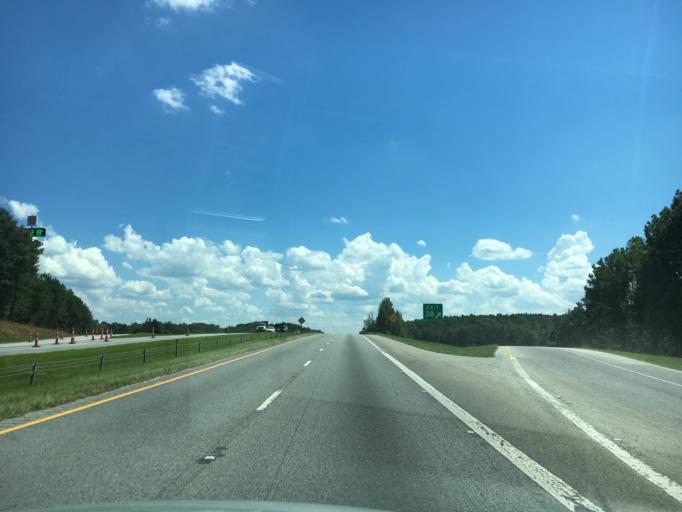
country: US
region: South Carolina
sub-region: Spartanburg County
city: Woodruff
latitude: 34.7013
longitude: -81.9414
